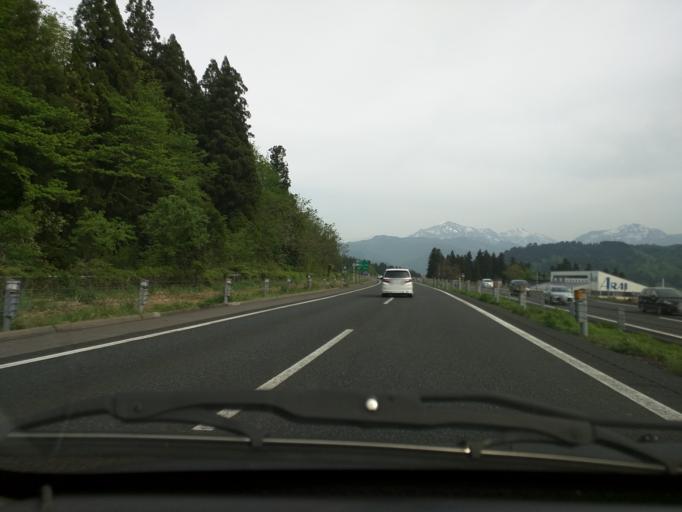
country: JP
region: Niigata
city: Ojiya
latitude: 37.2480
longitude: 138.9373
